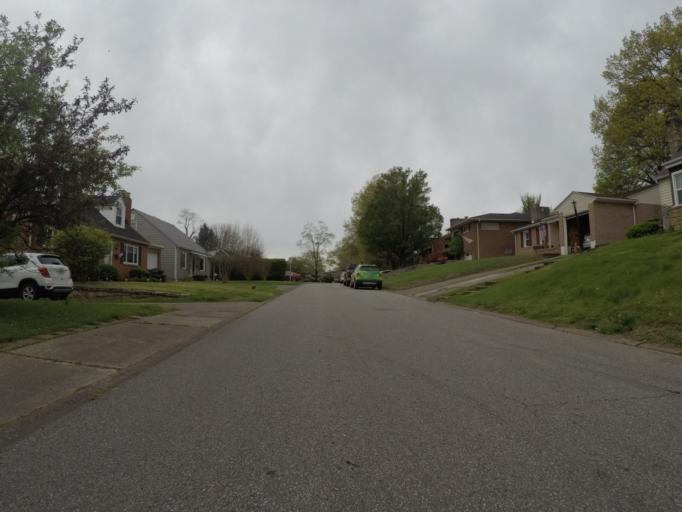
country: US
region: West Virginia
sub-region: Cabell County
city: Huntington
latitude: 38.4112
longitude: -82.3897
